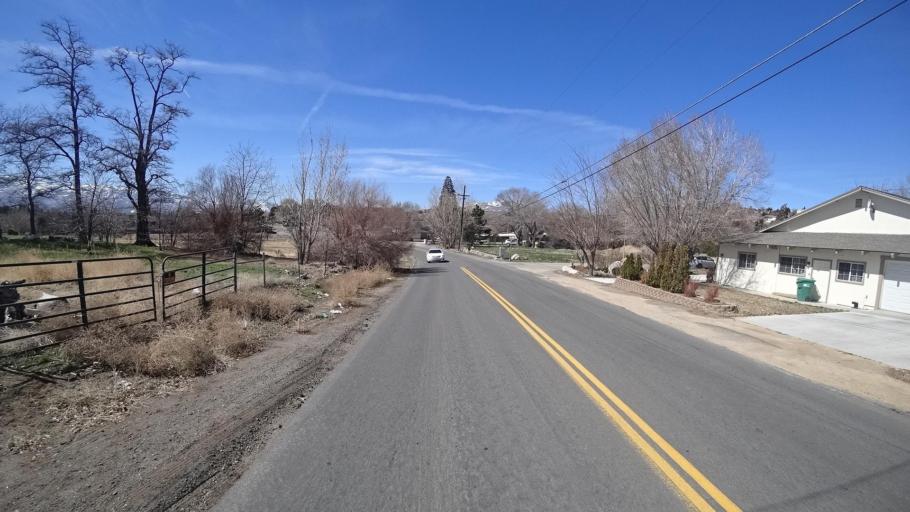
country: US
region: Nevada
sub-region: Washoe County
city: Sparks
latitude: 39.5538
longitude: -119.7772
